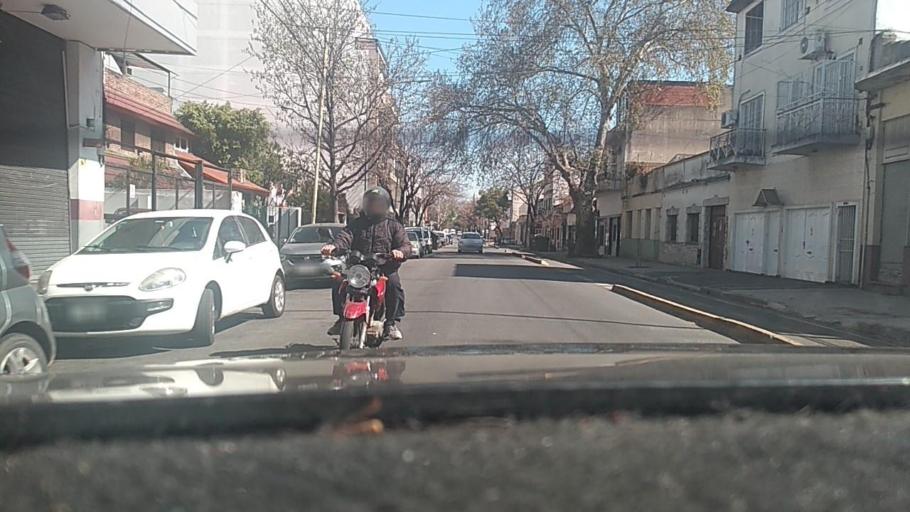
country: AR
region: Buenos Aires F.D.
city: Villa Santa Rita
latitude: -34.6134
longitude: -58.5049
